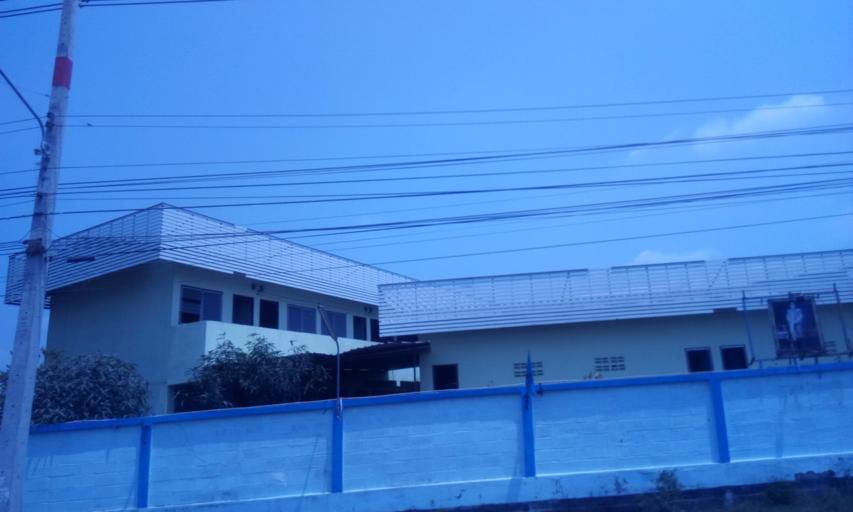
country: TH
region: Chachoengsao
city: Chachoengsao
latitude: 13.7596
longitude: 101.0736
